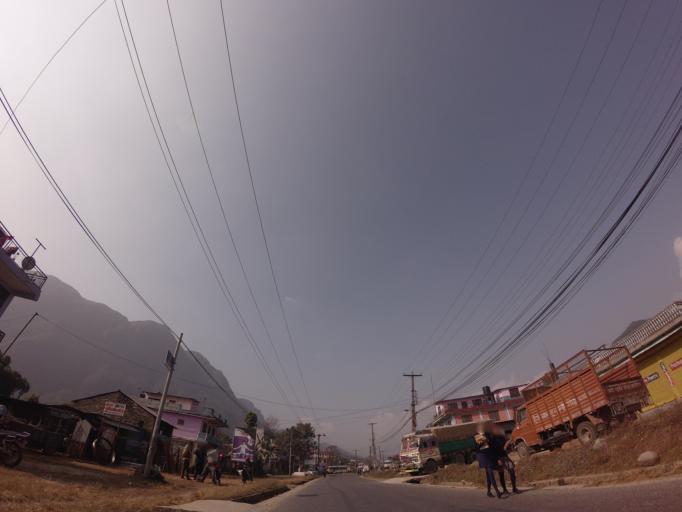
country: NP
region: Western Region
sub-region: Gandaki Zone
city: Pokhara
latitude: 28.2779
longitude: 83.9350
